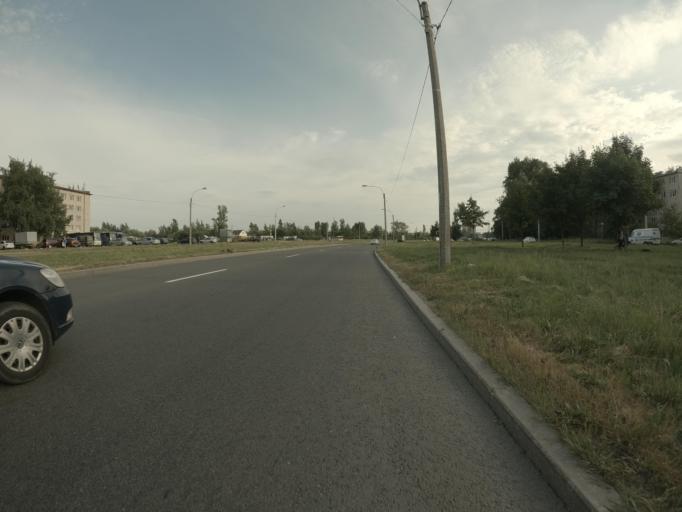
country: RU
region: Leningrad
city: Rybatskoye
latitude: 59.8826
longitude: 30.4880
